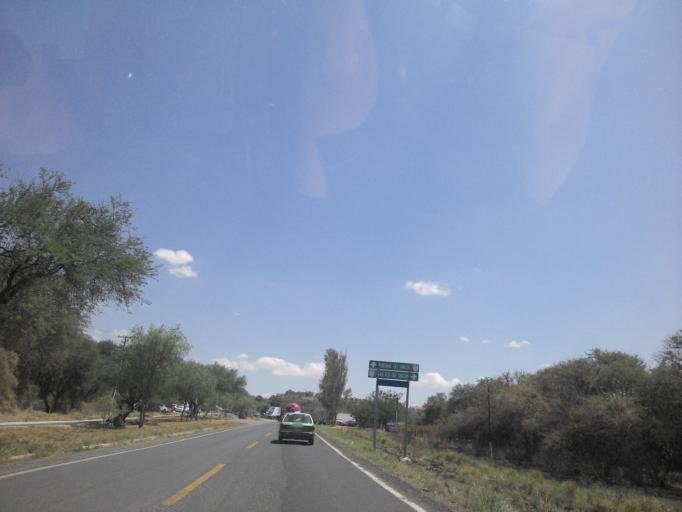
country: MX
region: Guanajuato
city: San Francisco del Rincon
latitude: 21.0245
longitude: -101.8909
